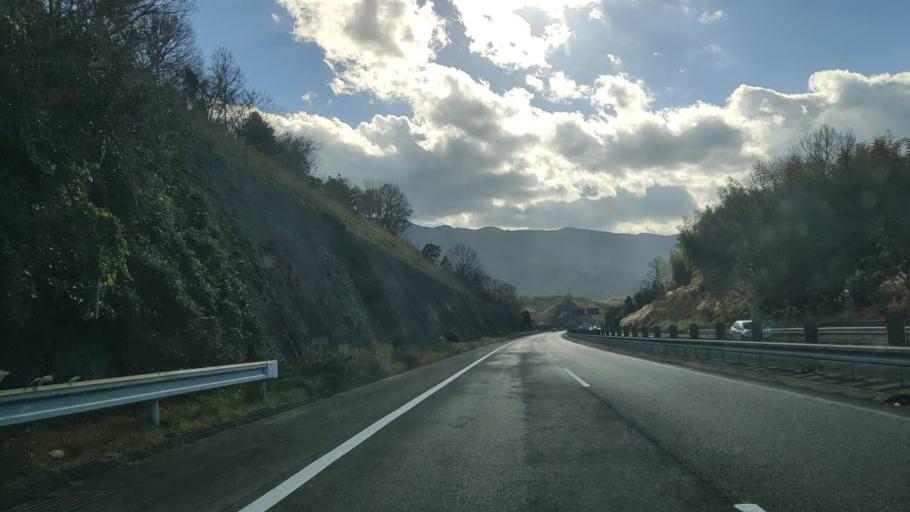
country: JP
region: Ehime
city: Kawanoecho
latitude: 33.9948
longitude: 133.5956
